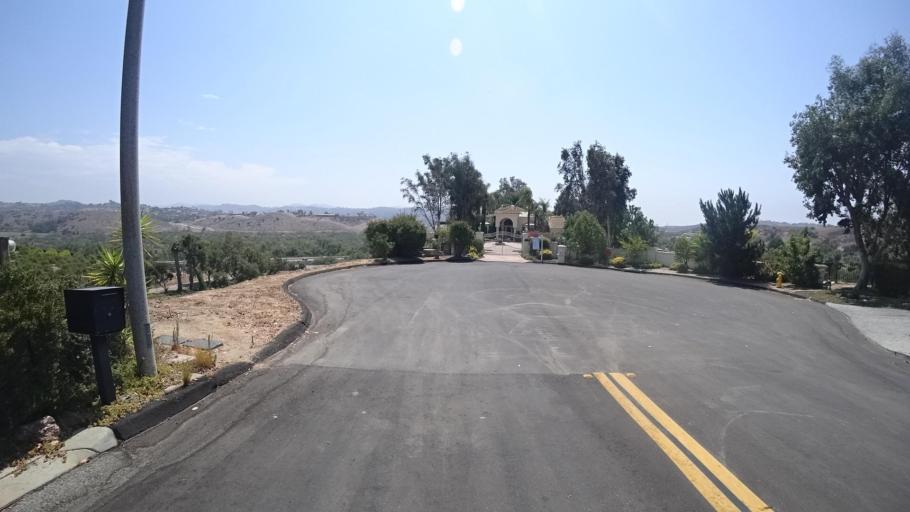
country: US
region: California
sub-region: San Diego County
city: Bonsall
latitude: 33.3049
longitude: -117.2173
